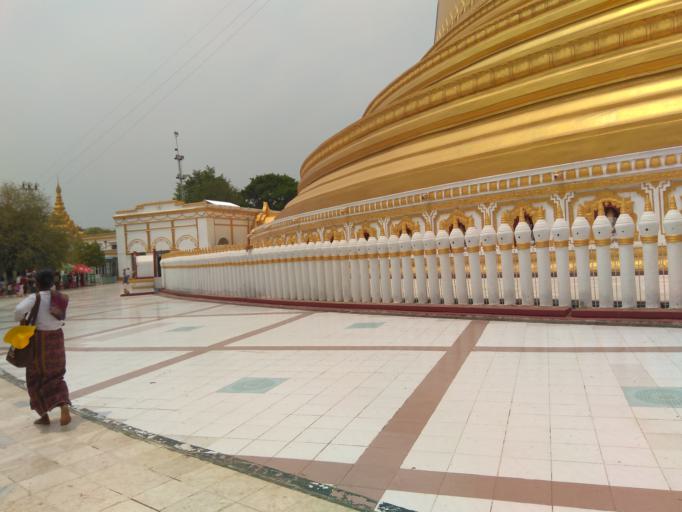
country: MM
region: Sagain
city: Sagaing
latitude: 21.9327
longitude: 95.9385
